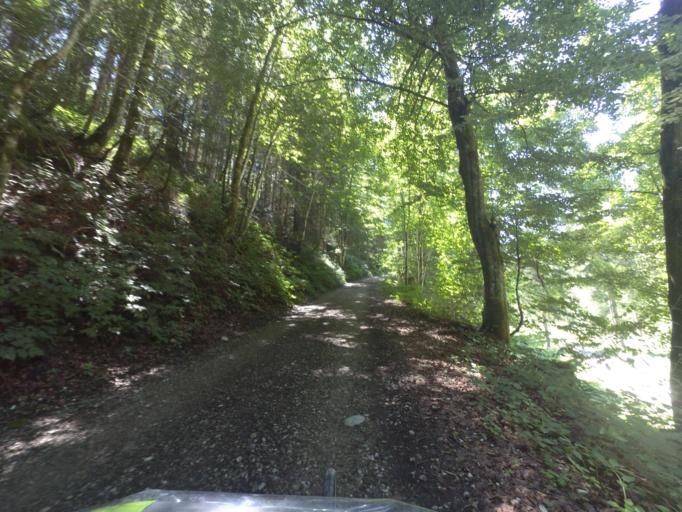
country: AT
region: Salzburg
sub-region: Politischer Bezirk Salzburg-Umgebung
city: Hintersee
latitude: 47.7074
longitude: 13.2839
